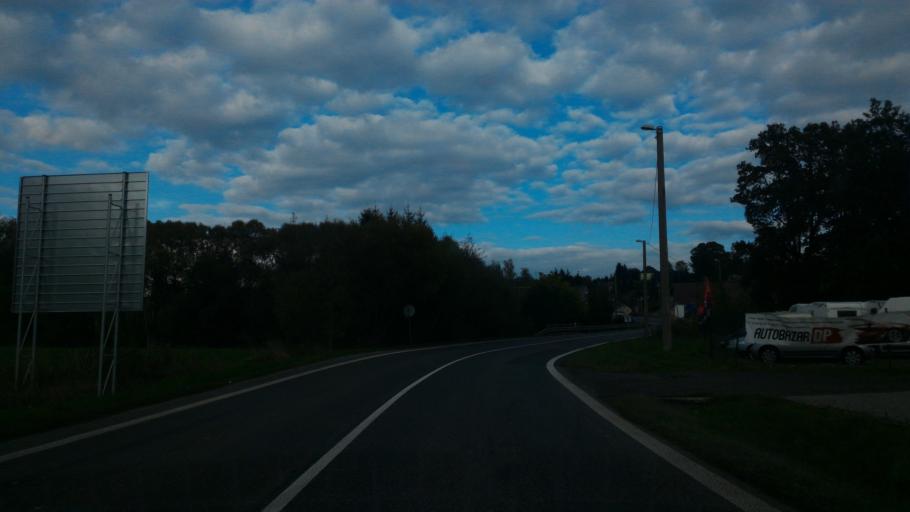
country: CZ
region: Ustecky
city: Ceska Kamenice
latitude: 50.7866
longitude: 14.3677
